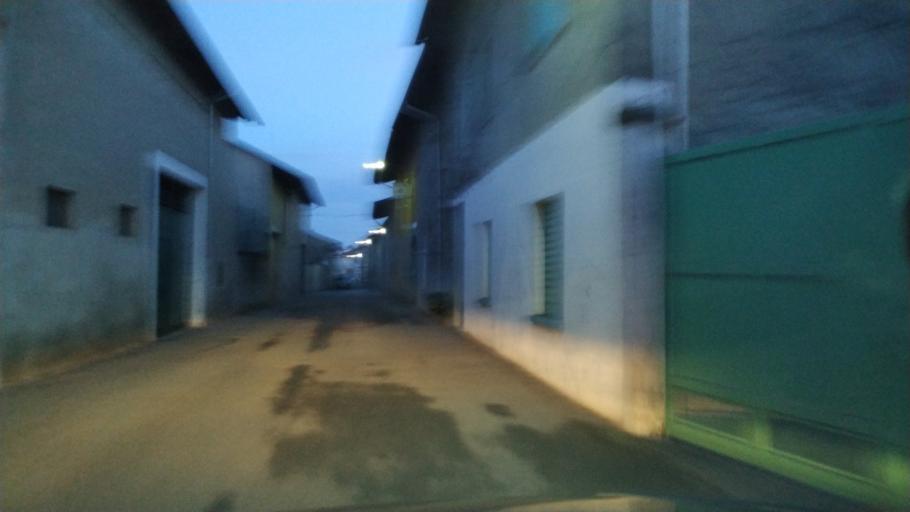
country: IT
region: Piedmont
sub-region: Provincia di Vercelli
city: Borgo d'Ale
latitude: 45.3482
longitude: 8.0493
